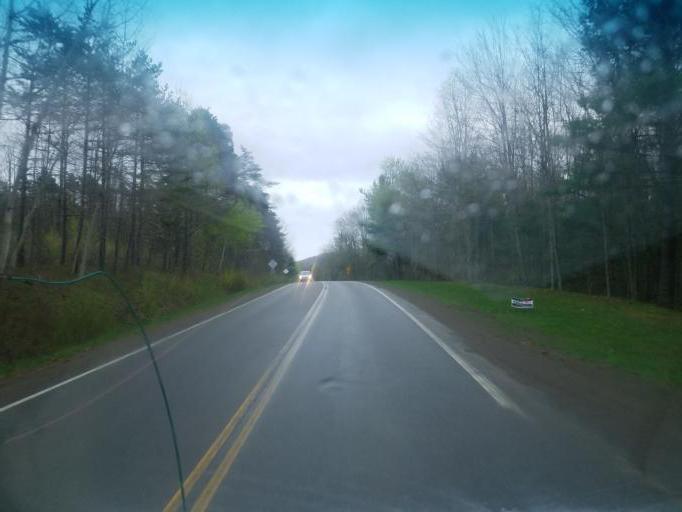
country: US
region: New York
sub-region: Allegany County
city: Belmont
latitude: 42.1713
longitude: -78.0581
